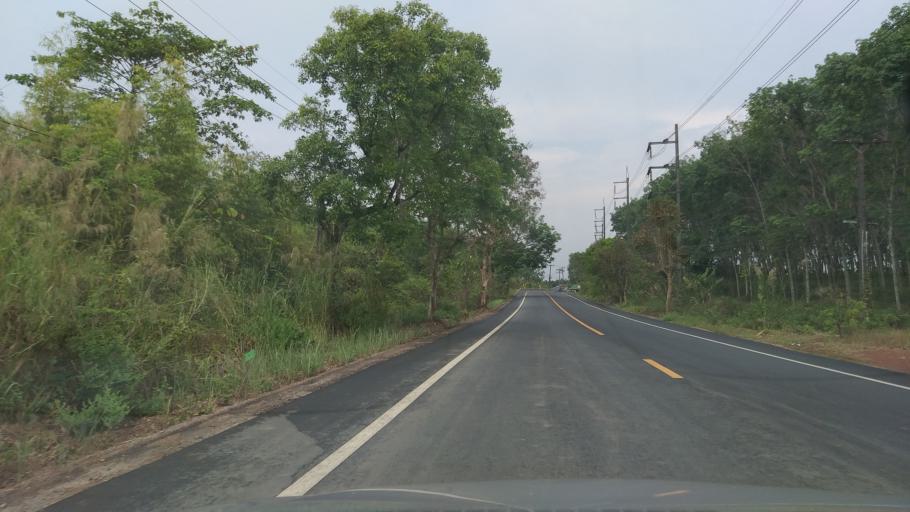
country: TH
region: Trat
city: Khao Saming
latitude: 12.3332
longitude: 102.3701
